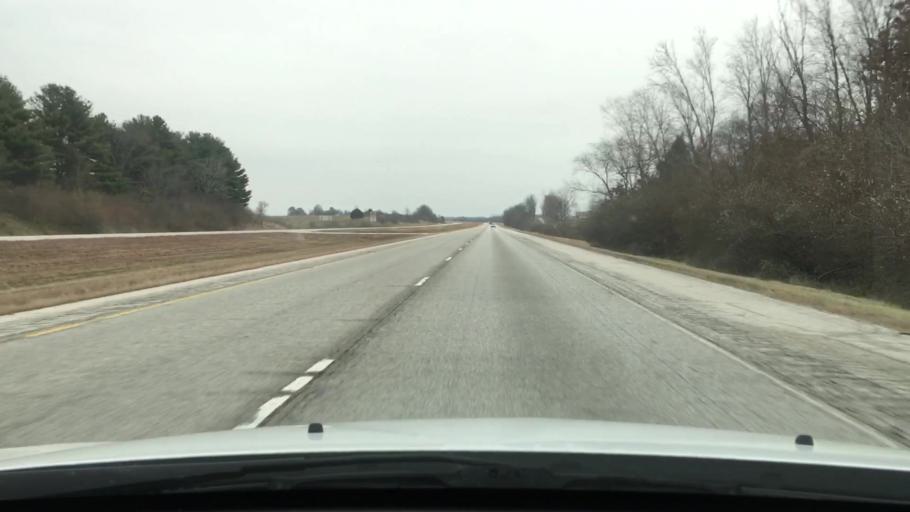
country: US
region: Illinois
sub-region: Morgan County
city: South Jacksonville
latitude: 39.6803
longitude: -90.2814
